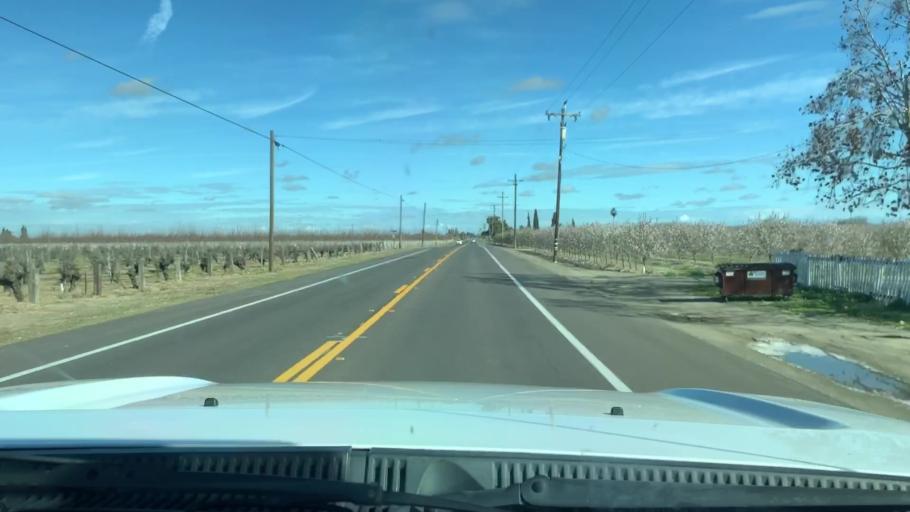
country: US
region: California
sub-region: Fresno County
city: Selma
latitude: 36.5317
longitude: -119.6829
